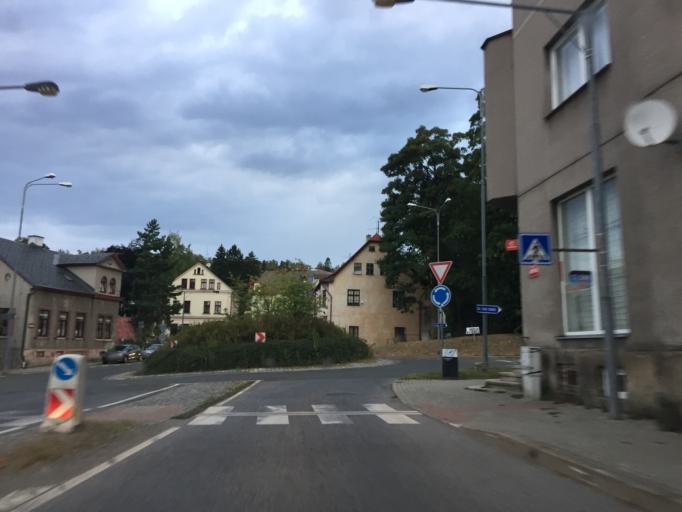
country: CZ
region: Liberecky
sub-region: Okres Jablonec nad Nisou
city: Jablonec nad Nisou
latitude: 50.7034
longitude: 15.1858
